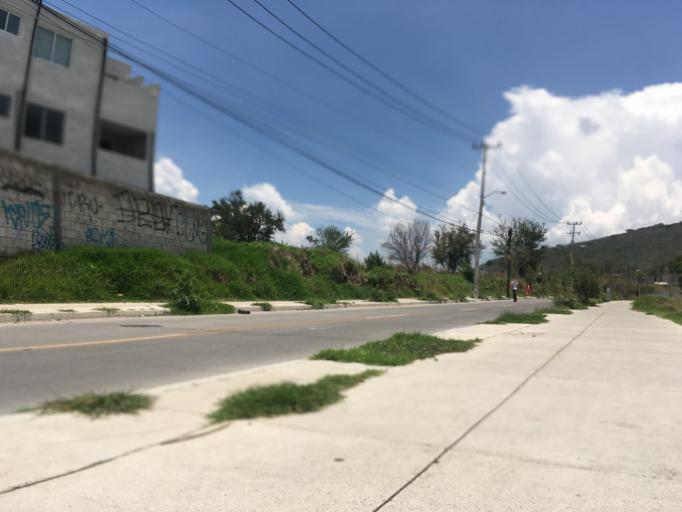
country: MX
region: Jalisco
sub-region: Tlajomulco de Zuniga
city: La Roca
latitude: 20.5157
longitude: -103.4259
